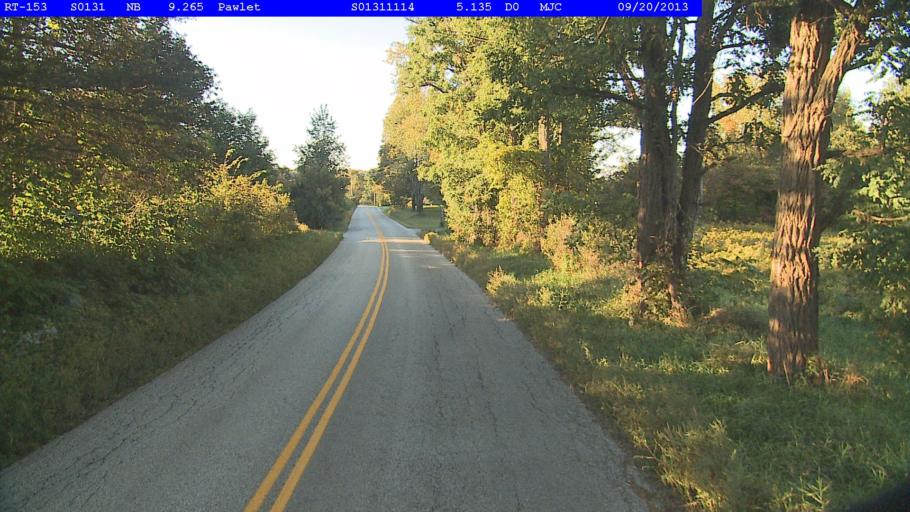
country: US
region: New York
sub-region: Washington County
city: Granville
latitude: 43.3779
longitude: -73.2255
